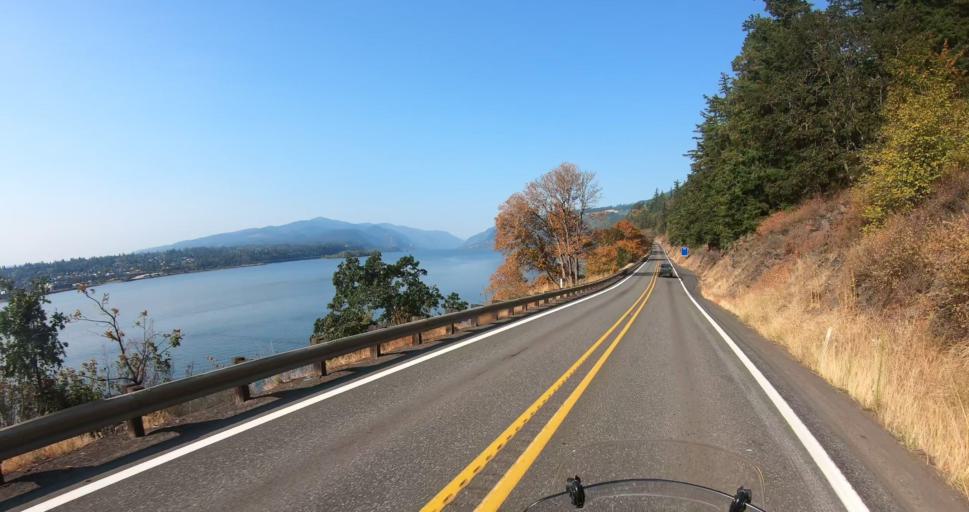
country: US
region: Washington
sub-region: Klickitat County
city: White Salmon
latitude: 45.7268
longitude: -121.5058
